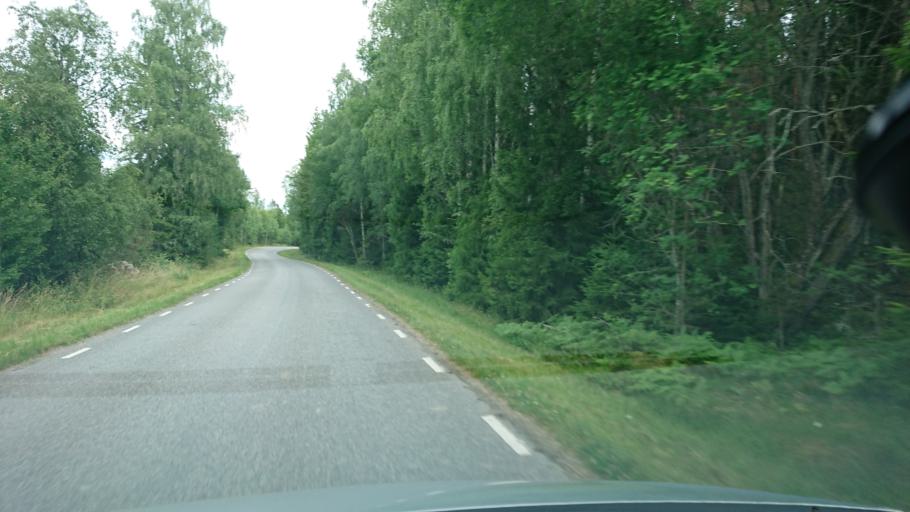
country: SE
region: Uppsala
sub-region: Osthammars Kommun
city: Bjorklinge
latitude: 60.0056
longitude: 17.4480
